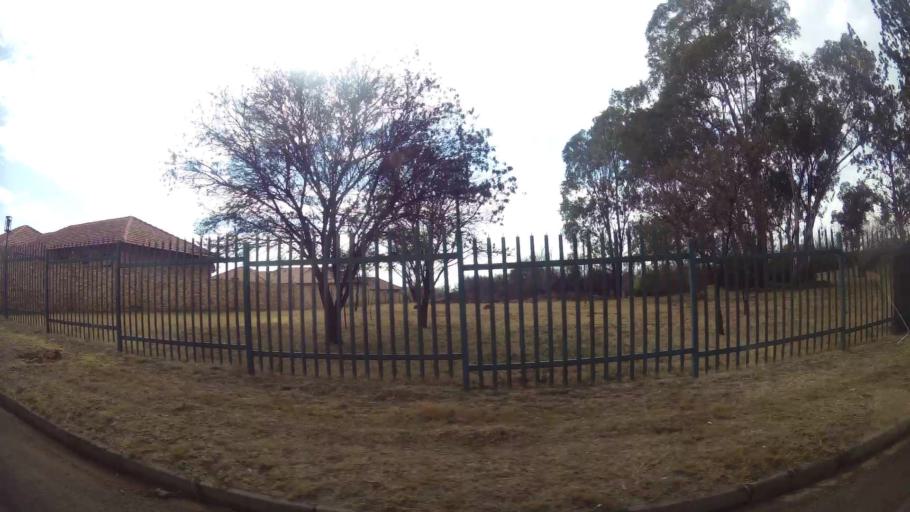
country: ZA
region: Gauteng
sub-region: Sedibeng District Municipality
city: Meyerton
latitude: -26.5852
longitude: 28.0129
